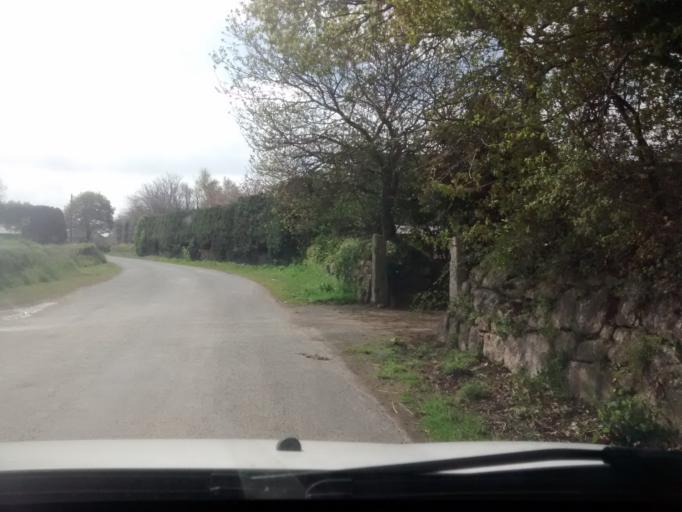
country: FR
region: Brittany
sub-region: Departement des Cotes-d'Armor
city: Penvenan
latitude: 48.8246
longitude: -3.3117
